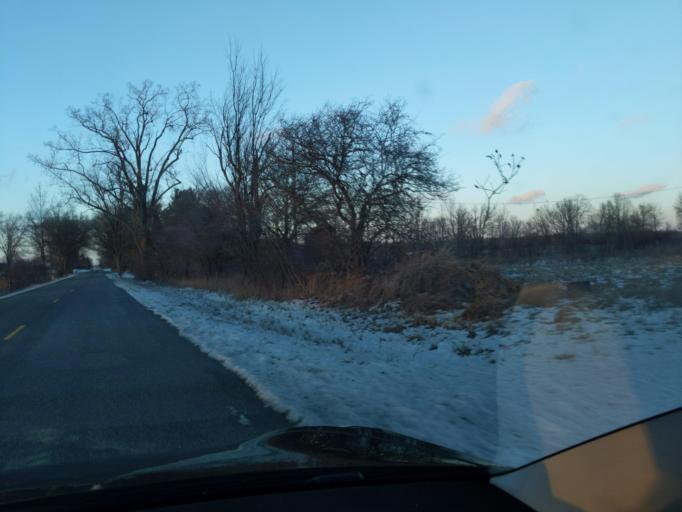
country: US
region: Michigan
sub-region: Ingham County
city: Stockbridge
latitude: 42.4592
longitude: -84.2779
